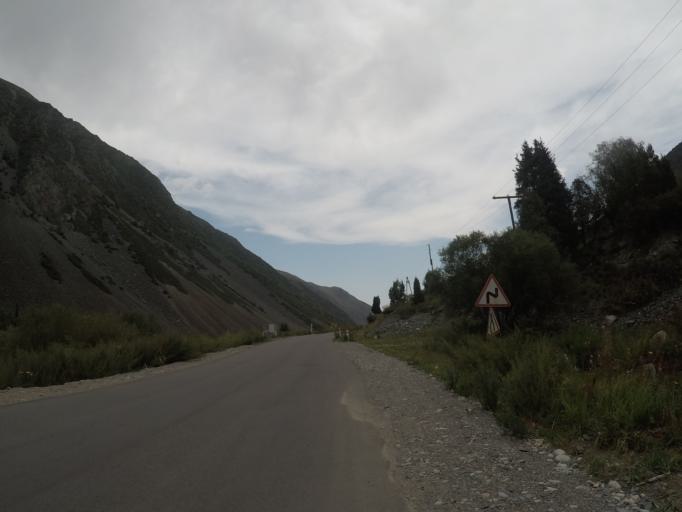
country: KG
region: Chuy
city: Bishkek
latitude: 42.5781
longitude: 74.4816
